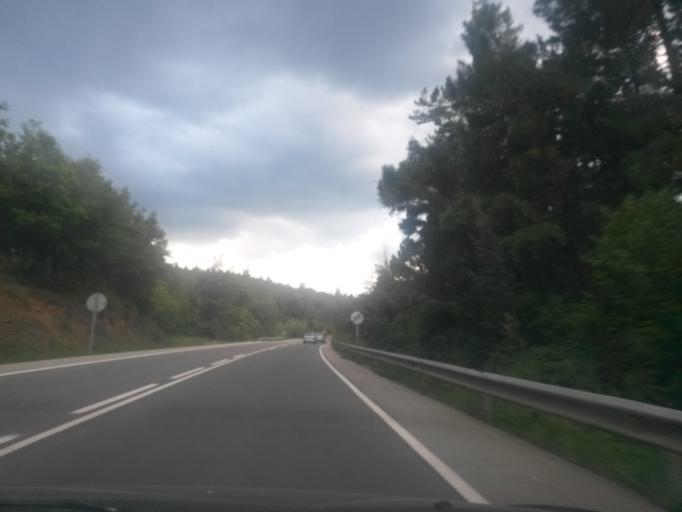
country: ES
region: Catalonia
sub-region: Provincia de Girona
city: Angles
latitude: 41.9463
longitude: 2.6419
